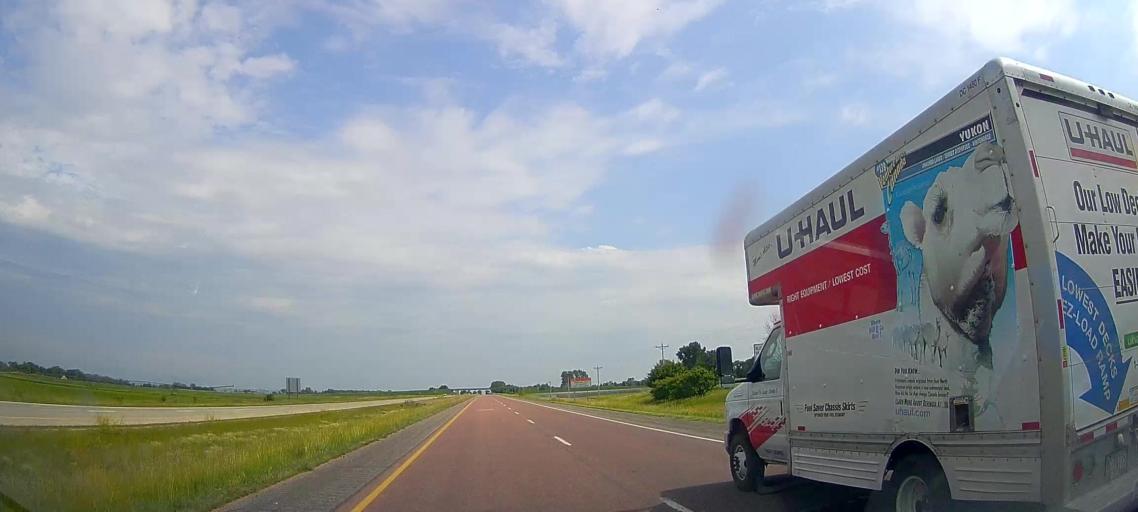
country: US
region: Iowa
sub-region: Monona County
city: Onawa
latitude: 41.9866
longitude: -96.1075
